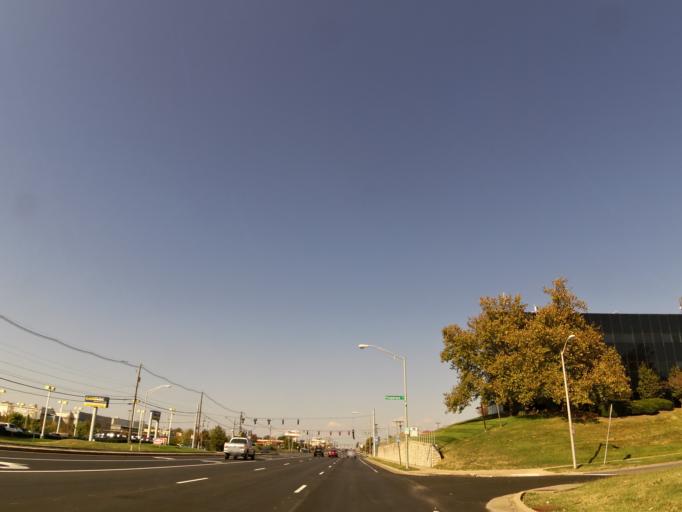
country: US
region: Kentucky
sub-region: Fayette County
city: Lexington
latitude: 38.0001
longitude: -84.4446
